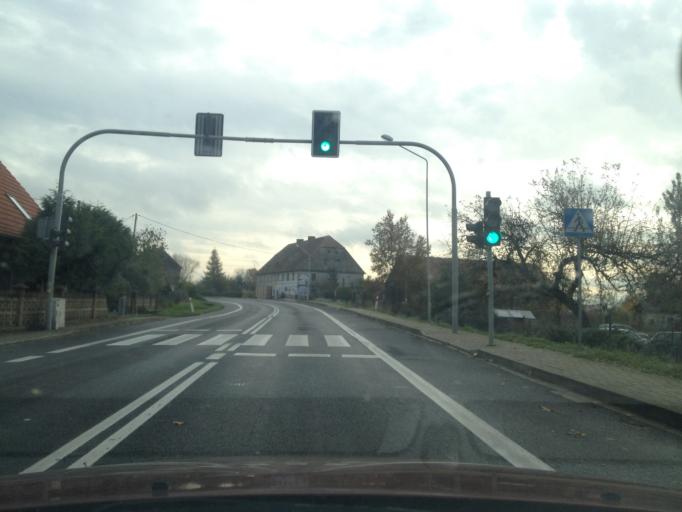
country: PL
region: Lower Silesian Voivodeship
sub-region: Powiat lubanski
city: Siekierczyn
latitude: 51.1487
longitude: 15.1731
